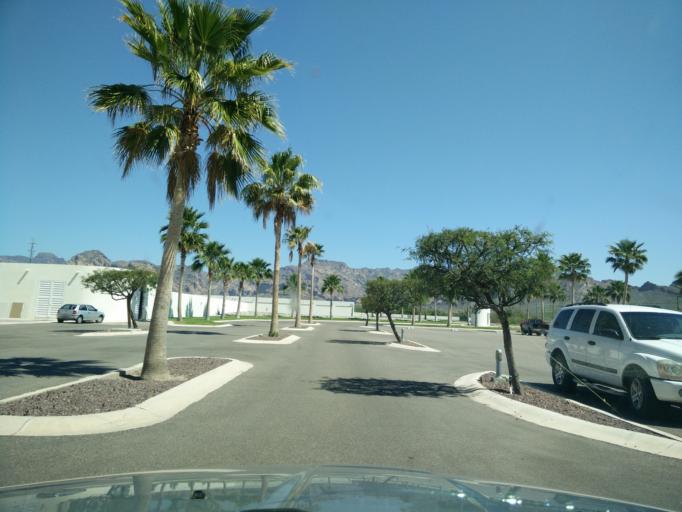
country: MX
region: Sonora
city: Heroica Guaymas
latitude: 27.9658
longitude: -111.1050
